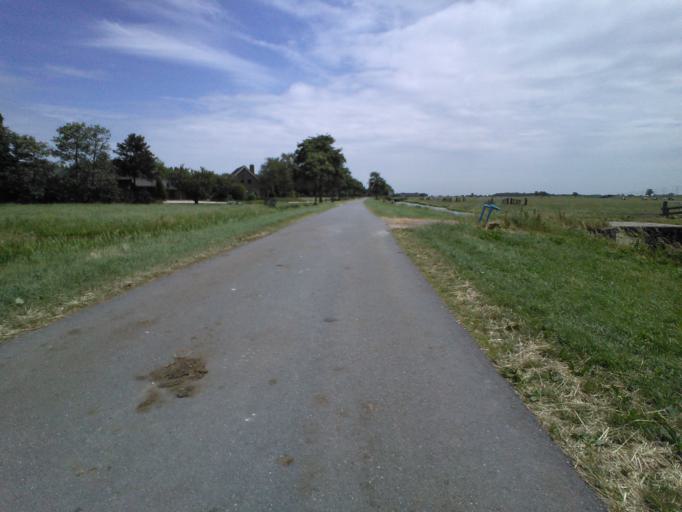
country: NL
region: South Holland
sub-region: Molenwaard
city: Nieuw-Lekkerland
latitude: 51.8817
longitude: 4.6867
